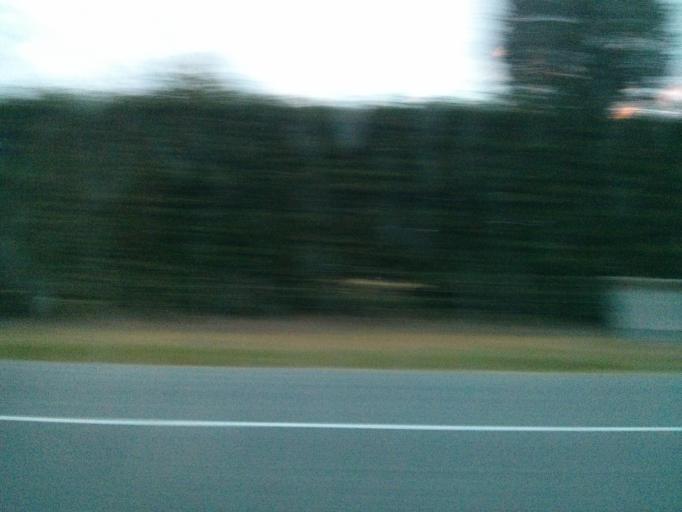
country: NZ
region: Canterbury
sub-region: Waimakariri District
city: Kaiapoi
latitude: -43.3847
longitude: 172.5551
